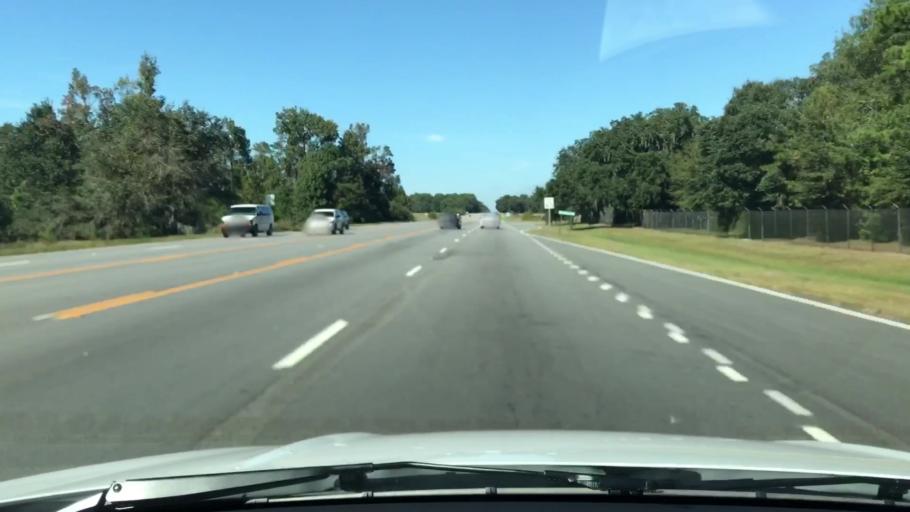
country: US
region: South Carolina
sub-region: Beaufort County
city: Burton
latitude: 32.4612
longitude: -80.7344
